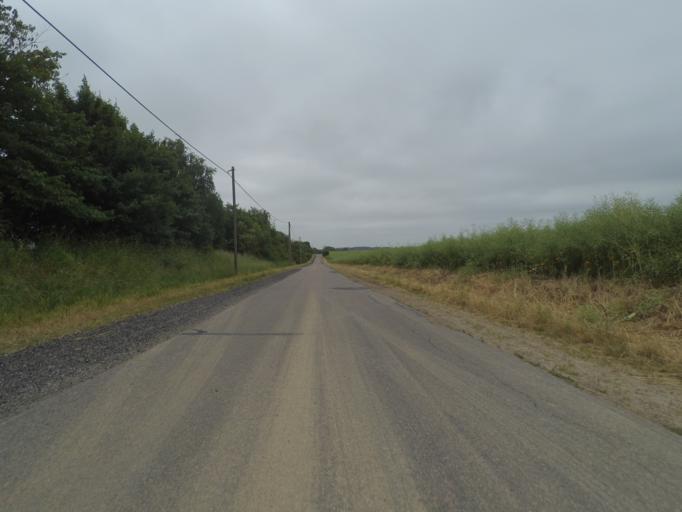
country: DE
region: Mecklenburg-Vorpommern
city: Gaegelow
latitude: 53.6999
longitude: 11.8671
